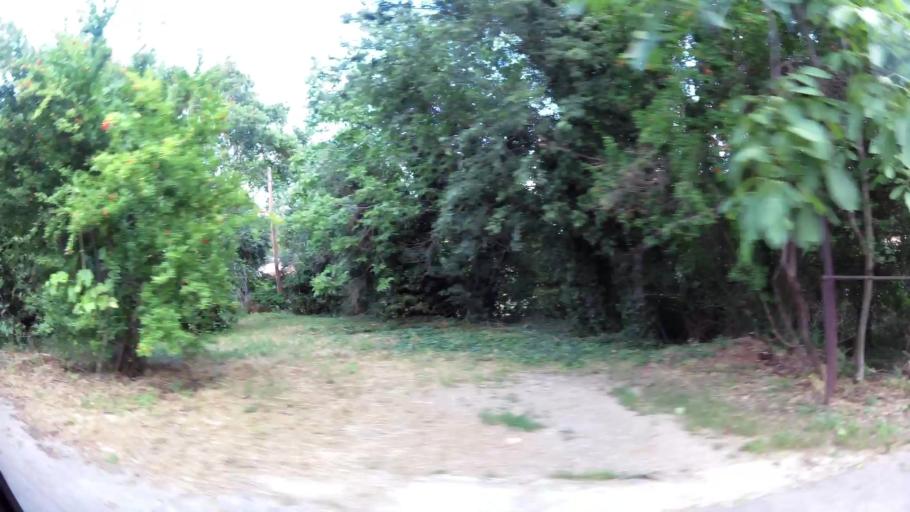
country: GR
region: Central Macedonia
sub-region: Nomos Thessalonikis
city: Pefka
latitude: 40.6582
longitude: 23.0034
